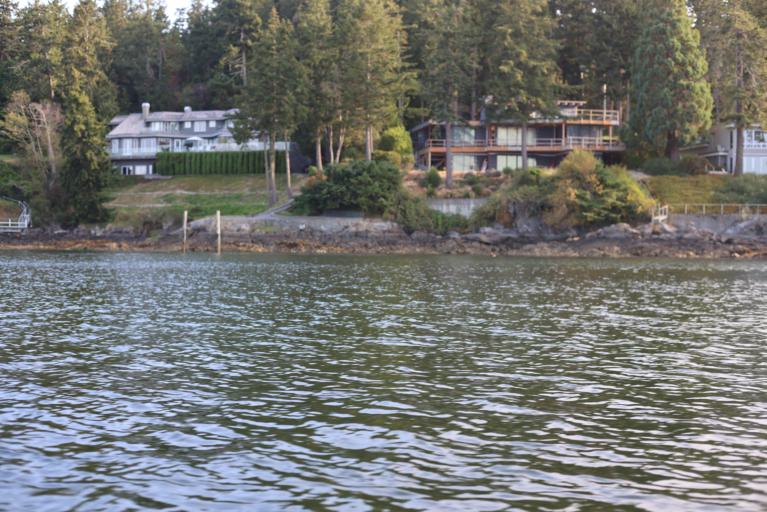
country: CA
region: British Columbia
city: North Saanich
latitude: 48.6738
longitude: -123.4050
